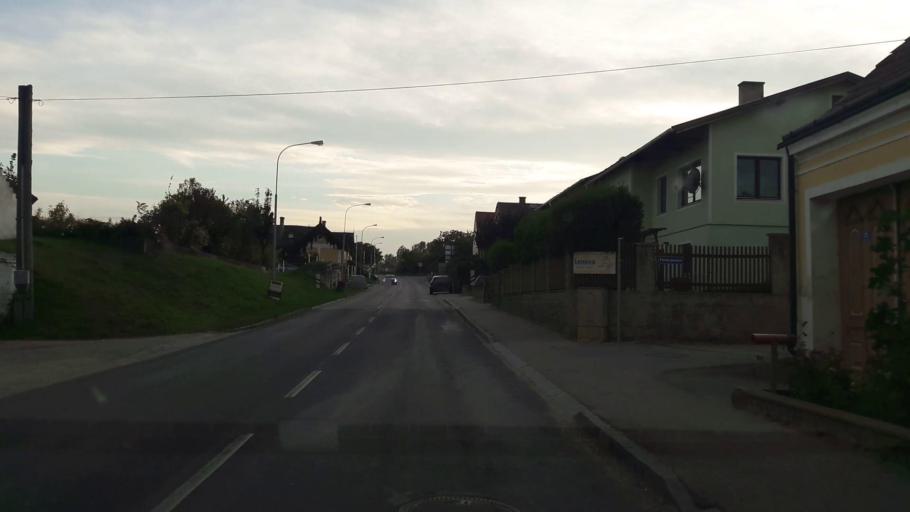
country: AT
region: Lower Austria
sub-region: Politischer Bezirk Korneuburg
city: Grossrussbach
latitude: 48.4767
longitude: 16.3826
